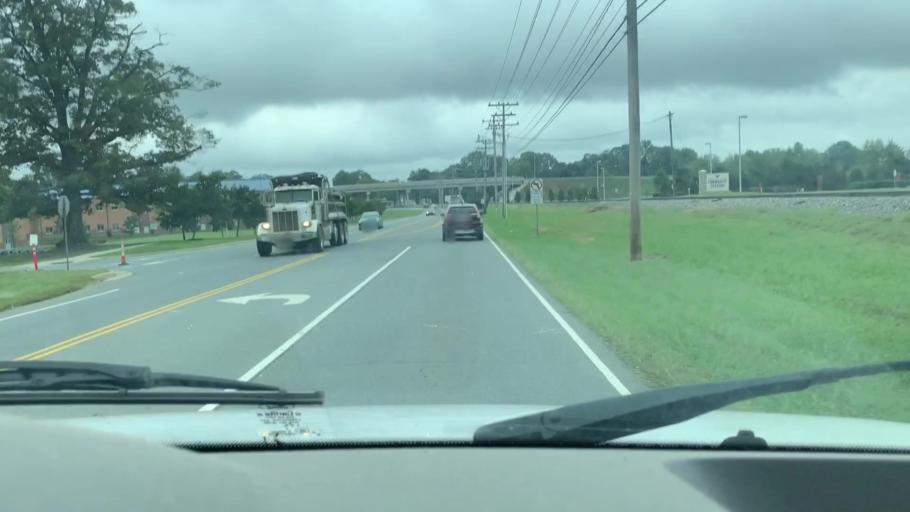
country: US
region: North Carolina
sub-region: Mecklenburg County
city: Huntersville
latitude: 35.3915
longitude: -80.8350
